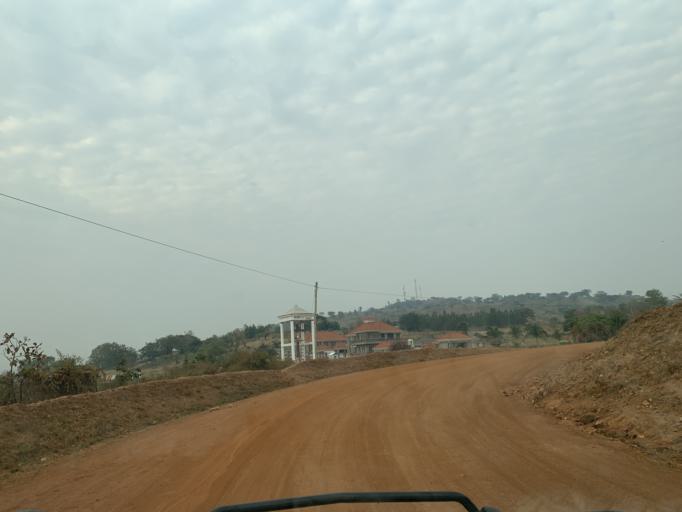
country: UG
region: Northern Region
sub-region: Nebbi District
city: Nebbi
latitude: 2.4746
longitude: 31.0736
